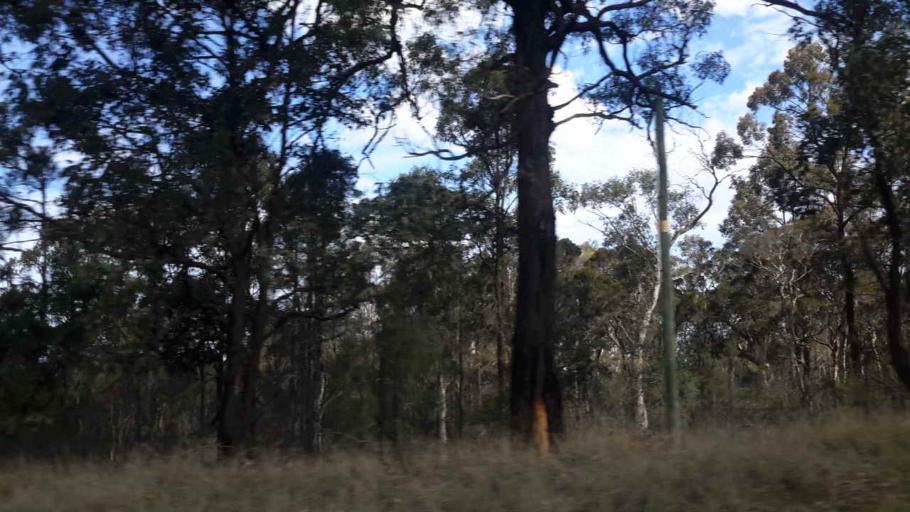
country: AU
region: New South Wales
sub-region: Hawkesbury
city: South Windsor
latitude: -33.6590
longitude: 150.7651
